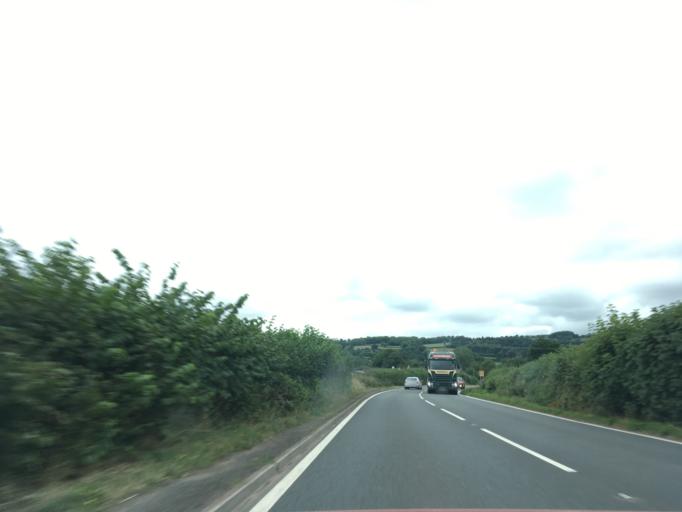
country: GB
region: Wales
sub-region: Sir Powys
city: Brecon
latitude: 51.9465
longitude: -3.4293
